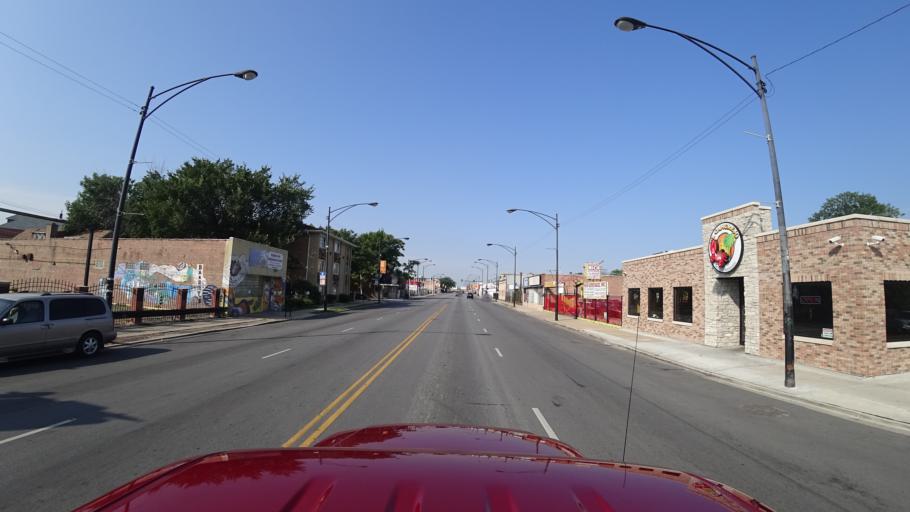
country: US
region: Illinois
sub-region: Cook County
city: Cicero
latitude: 41.8121
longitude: -87.7075
